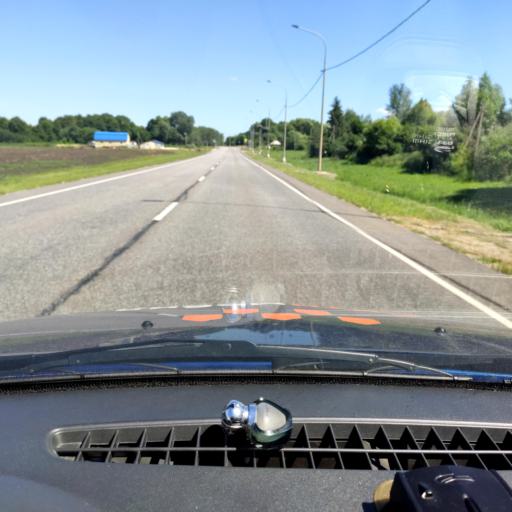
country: RU
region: Orjol
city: Pokrovskoye
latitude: 52.6200
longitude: 36.7364
